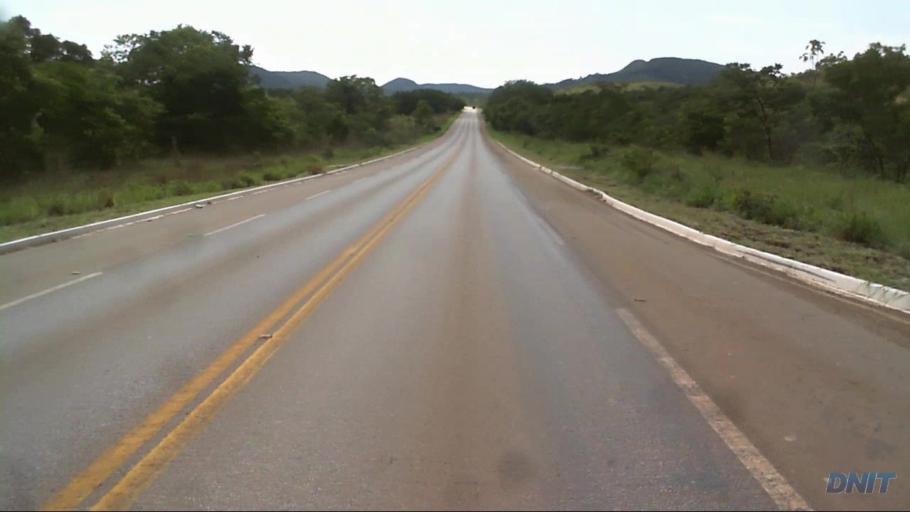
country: BR
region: Goias
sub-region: Barro Alto
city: Barro Alto
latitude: -15.1391
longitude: -48.8246
